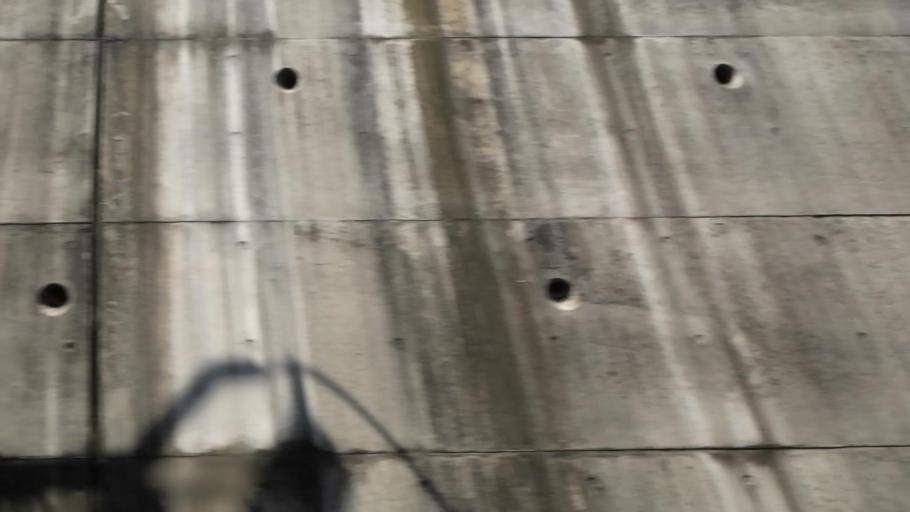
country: JP
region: Kagawa
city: Marugame
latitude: 34.2028
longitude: 133.8087
